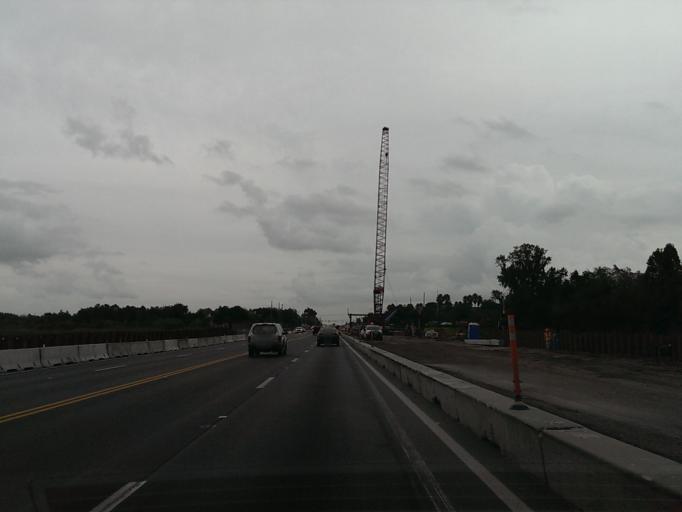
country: US
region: Florida
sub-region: Orange County
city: Ocoee
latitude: 28.5517
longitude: -81.5361
